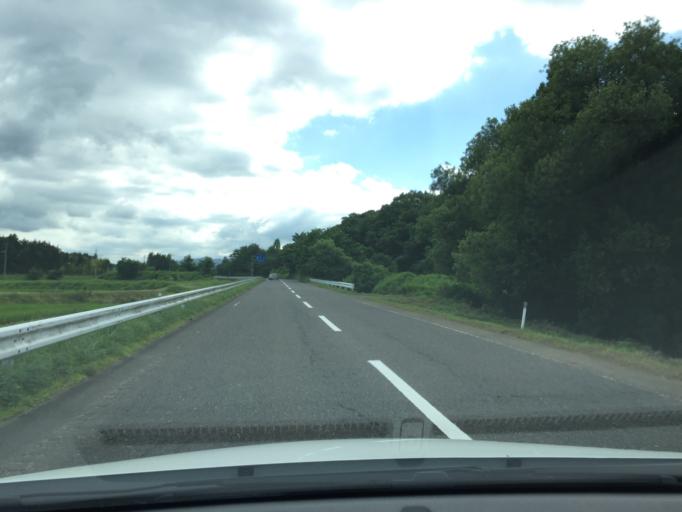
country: JP
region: Fukushima
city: Sukagawa
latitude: 37.3230
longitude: 140.2265
